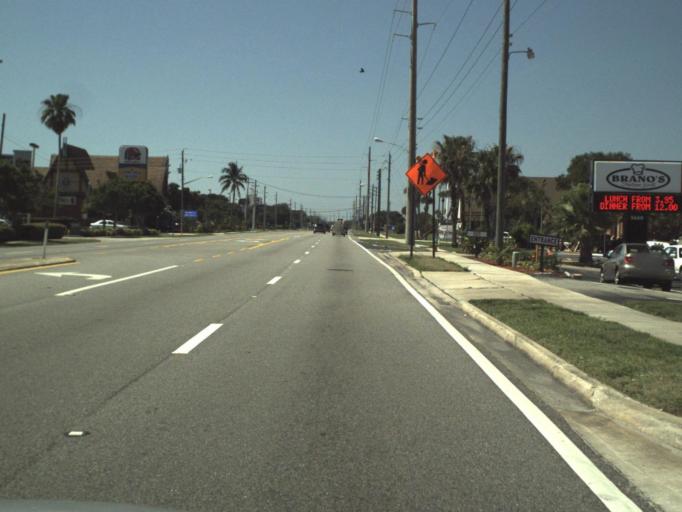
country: US
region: Florida
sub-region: Brevard County
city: Cocoa Beach
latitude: 28.3530
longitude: -80.6087
